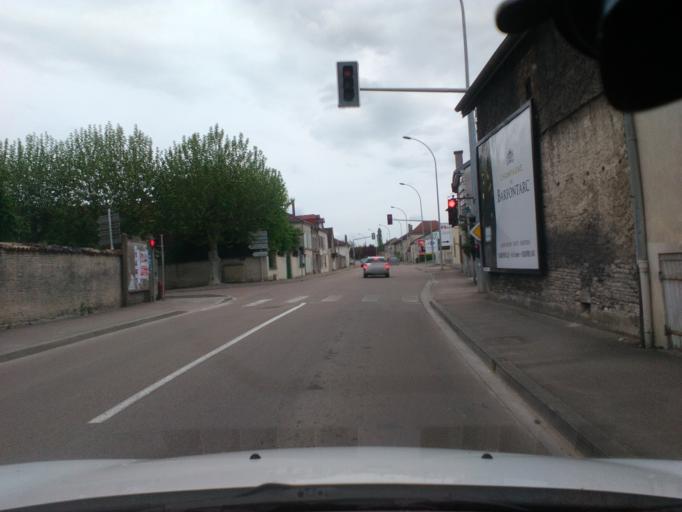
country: FR
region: Champagne-Ardenne
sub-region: Departement de l'Aube
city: Bar-sur-Aube
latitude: 48.2303
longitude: 4.7145
